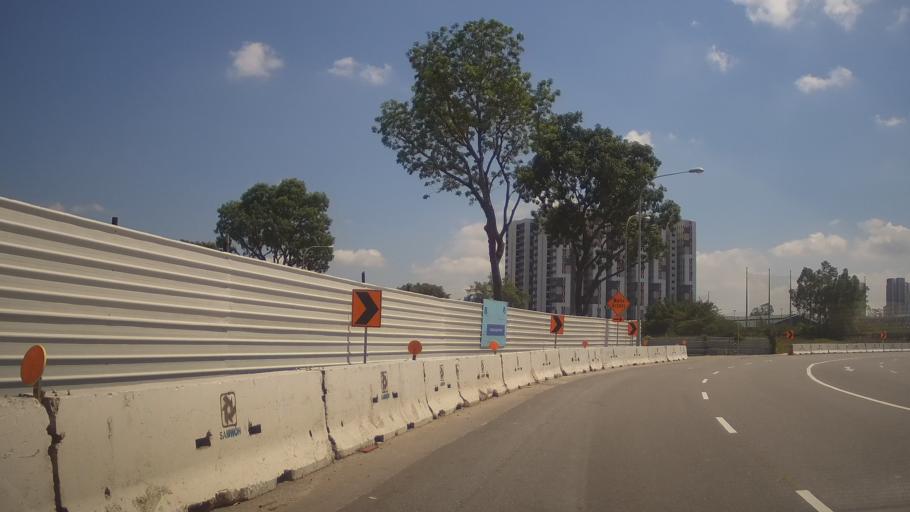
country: SG
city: Singapore
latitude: 1.3209
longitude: 103.7243
